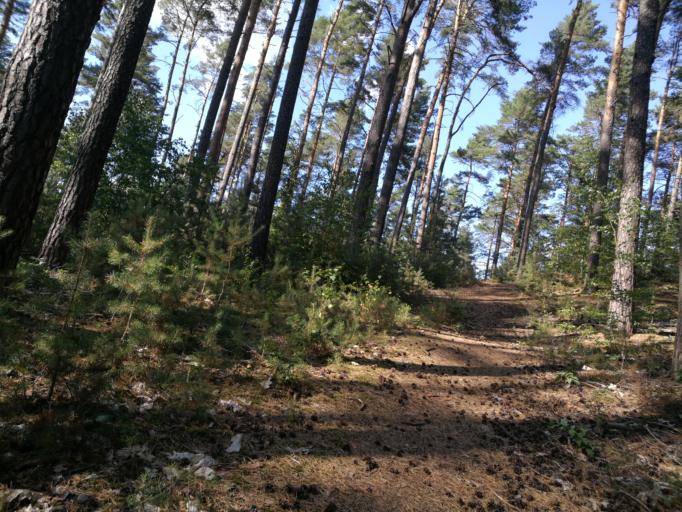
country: DE
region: Bavaria
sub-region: Regierungsbezirk Mittelfranken
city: Zirndorf
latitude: 49.4737
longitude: 10.9269
